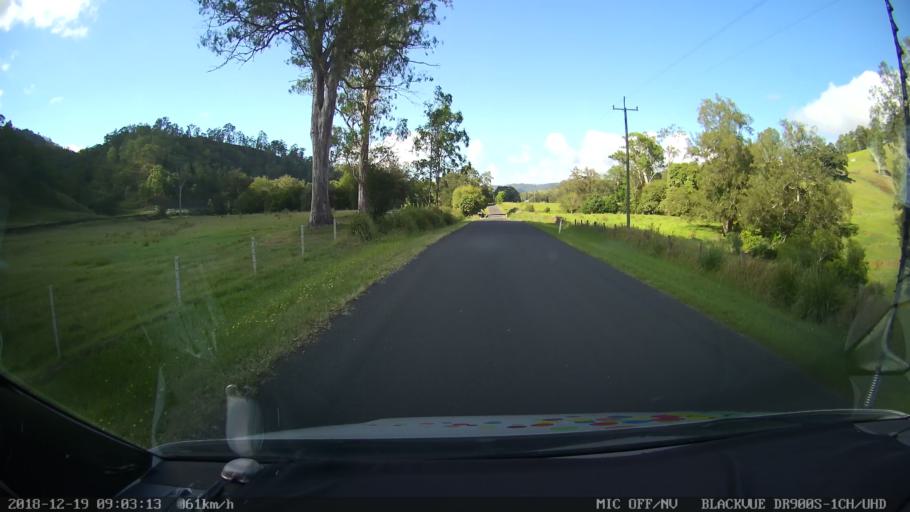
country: AU
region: New South Wales
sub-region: Kyogle
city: Kyogle
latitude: -28.4457
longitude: 152.9518
